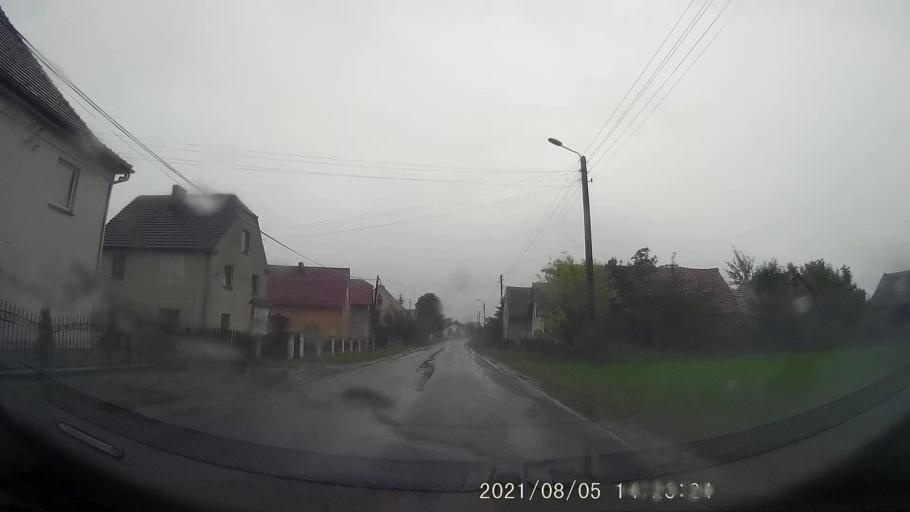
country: PL
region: Opole Voivodeship
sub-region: Powiat nyski
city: Korfantow
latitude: 50.4816
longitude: 17.6479
